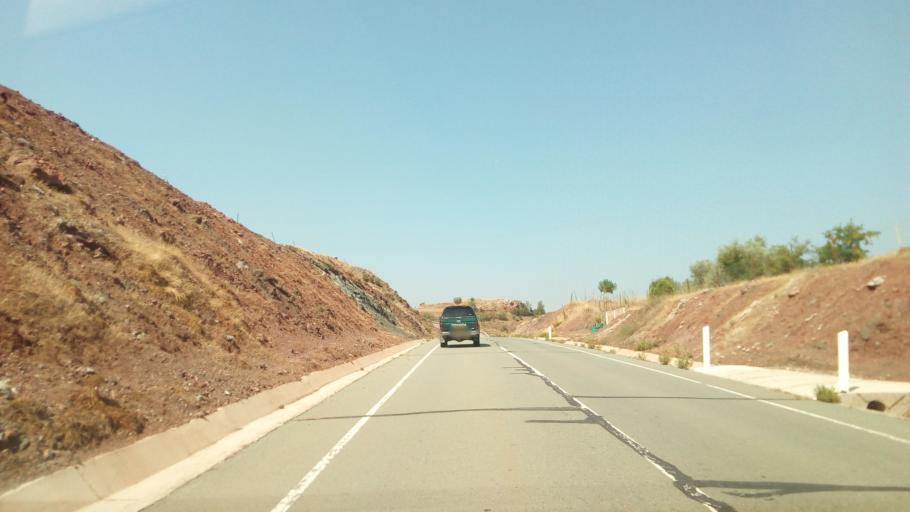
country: CY
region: Limassol
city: Pissouri
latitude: 34.7721
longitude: 32.6059
